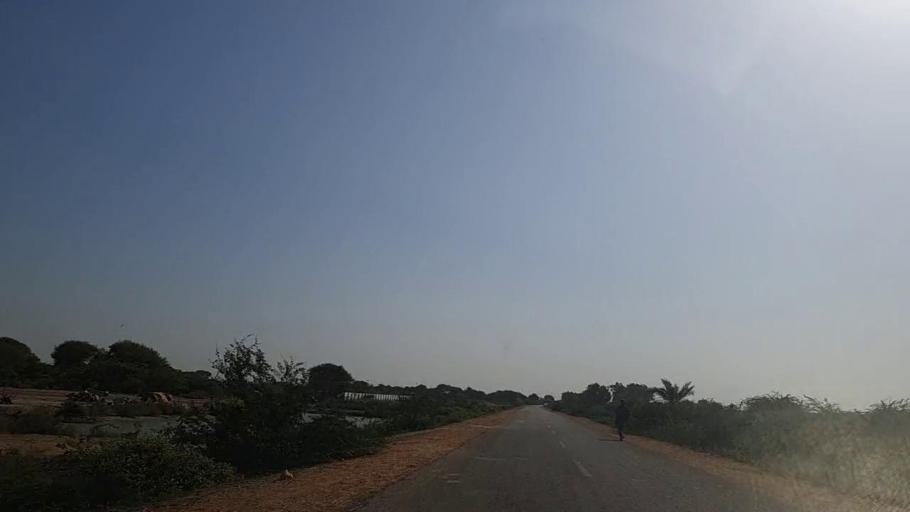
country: PK
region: Sindh
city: Jati
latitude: 24.4282
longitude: 68.2585
